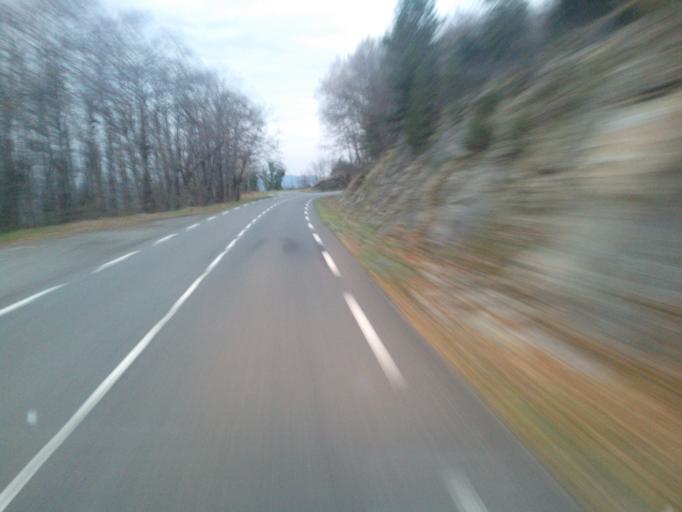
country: FR
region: Languedoc-Roussillon
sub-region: Departement du Gard
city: Valleraugue
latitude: 44.1659
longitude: 3.7180
